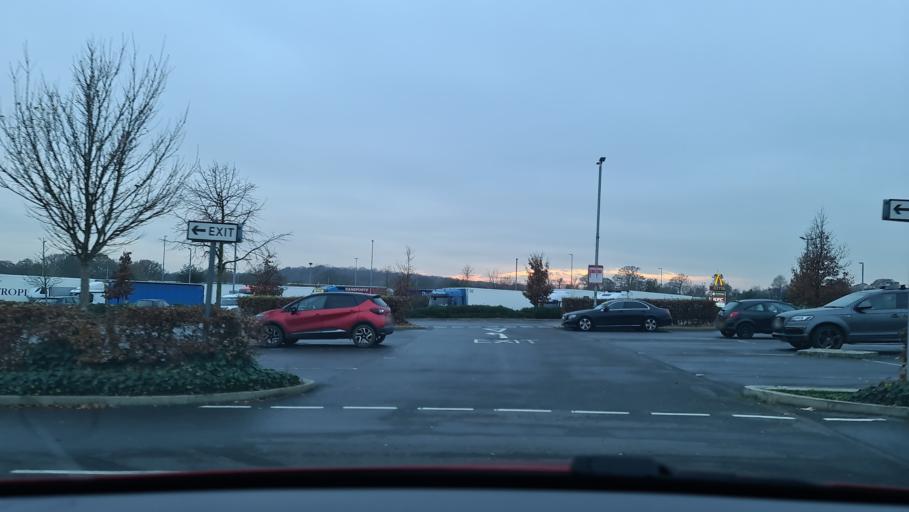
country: GB
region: England
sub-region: Surrey
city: Cobham
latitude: 51.3053
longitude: -0.4062
